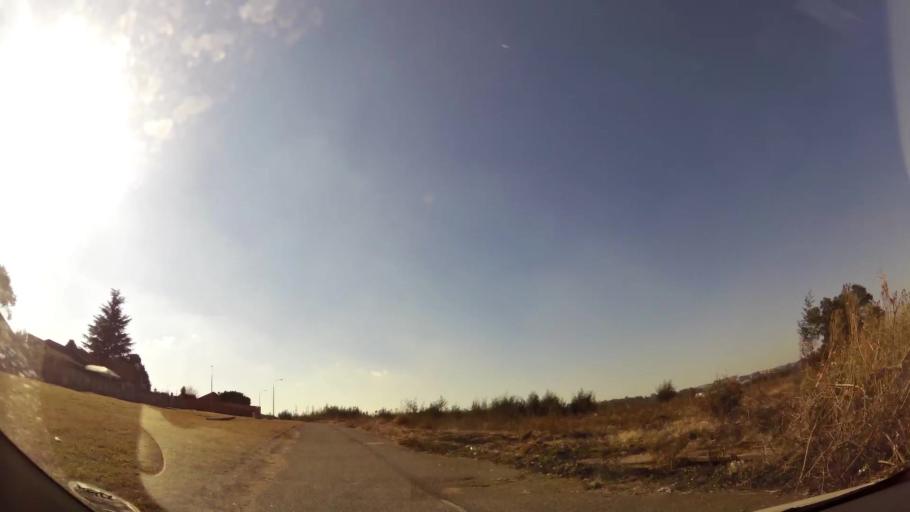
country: ZA
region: Gauteng
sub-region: City of Johannesburg Metropolitan Municipality
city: Roodepoort
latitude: -26.1684
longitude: 27.8273
